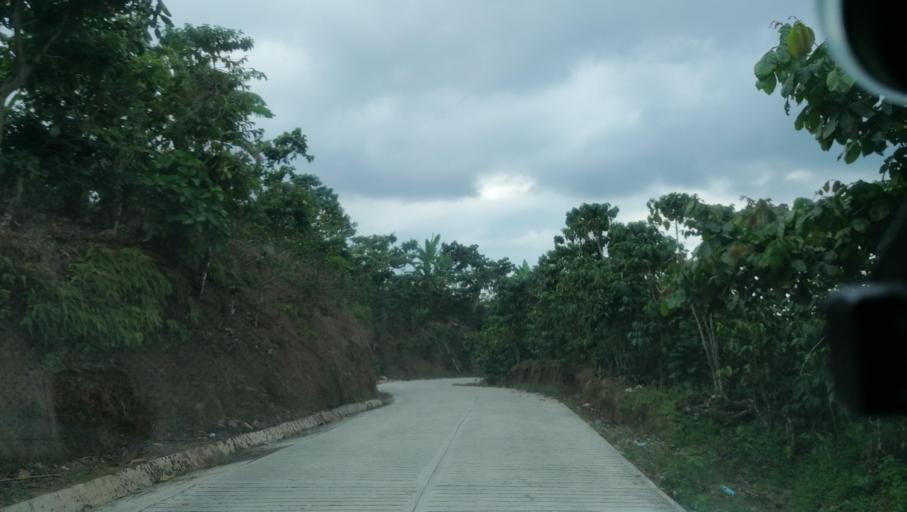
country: MX
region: Chiapas
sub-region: Cacahoatan
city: Benito Juarez
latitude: 15.0768
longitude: -92.1620
